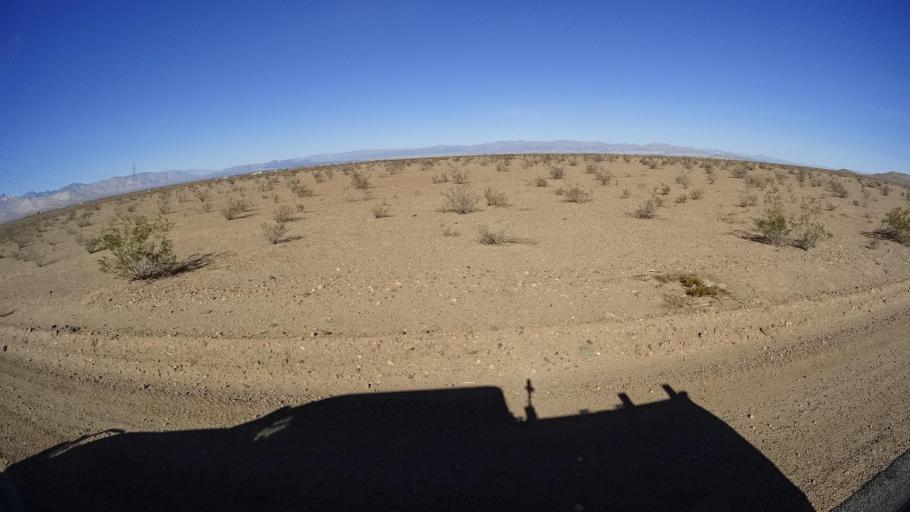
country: US
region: California
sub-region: Kern County
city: China Lake Acres
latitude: 35.5591
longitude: -117.7597
